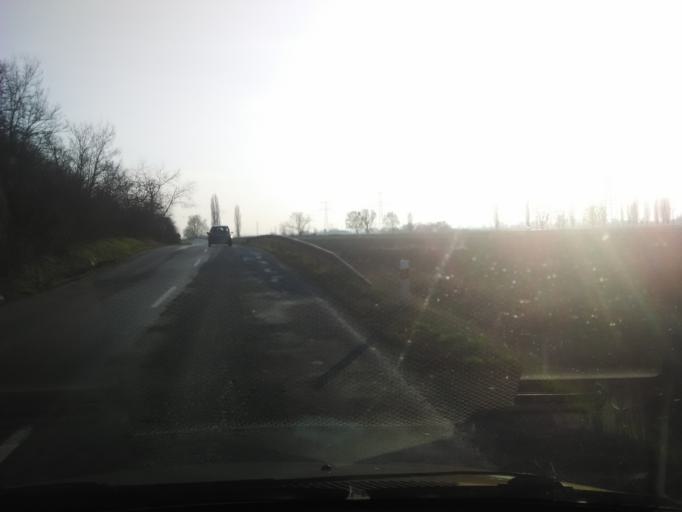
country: SK
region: Nitriansky
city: Levice
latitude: 48.2416
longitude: 18.5985
